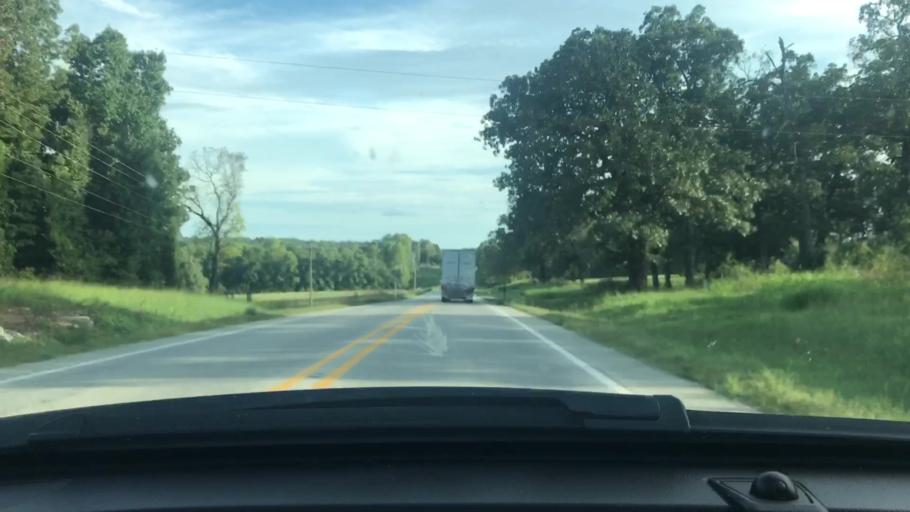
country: US
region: Arkansas
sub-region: Randolph County
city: Pocahontas
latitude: 36.1607
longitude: -91.1621
